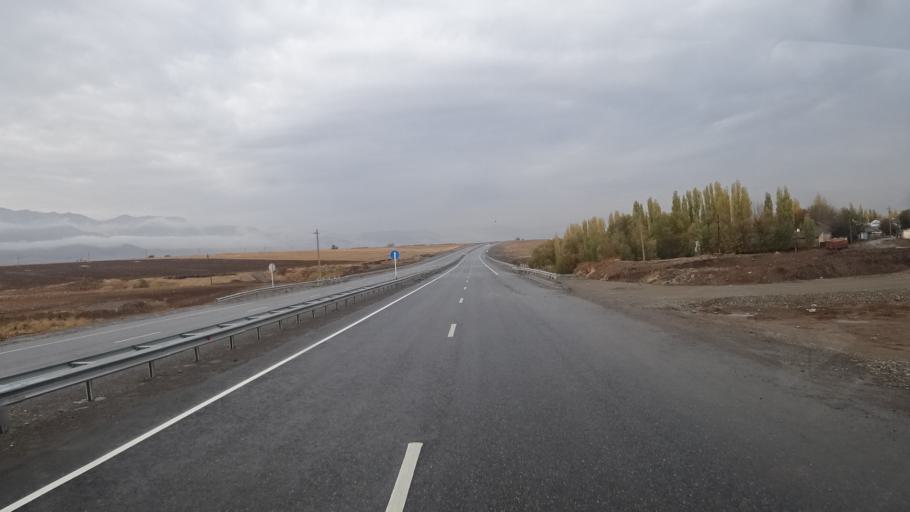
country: KZ
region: Ongtustik Qazaqstan
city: Turar Ryskulov
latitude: 42.5151
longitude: 70.3466
